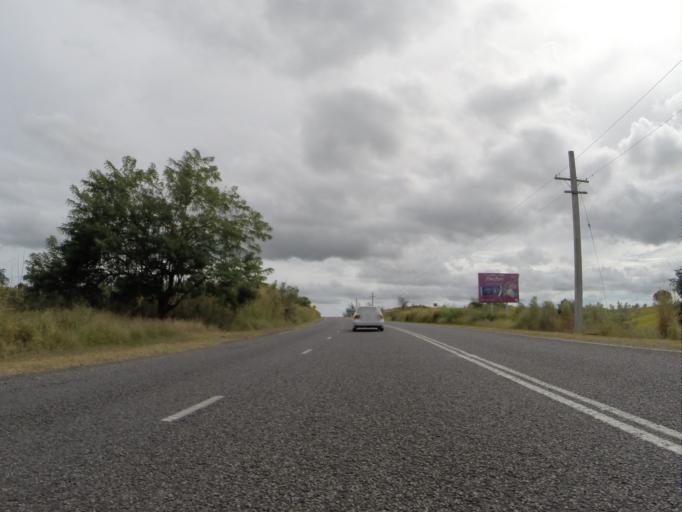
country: FJ
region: Western
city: Nadi
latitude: -18.0347
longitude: 177.3345
